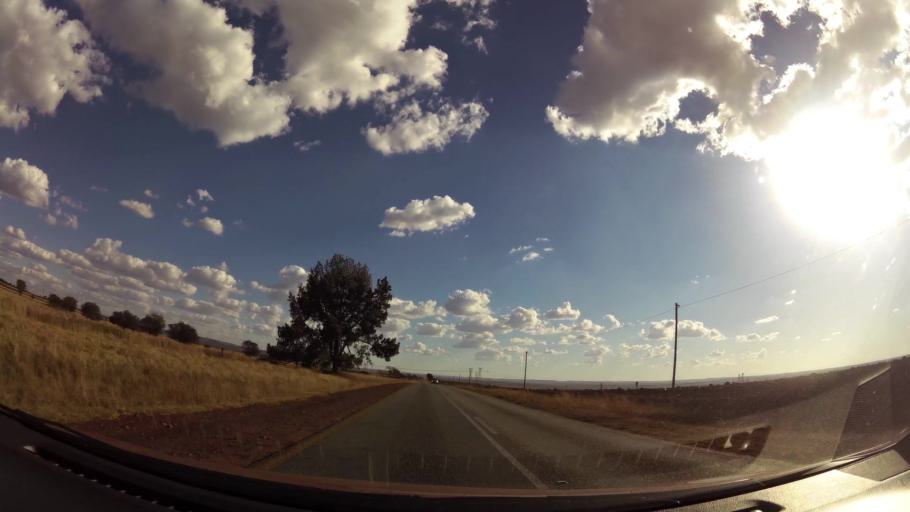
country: ZA
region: Gauteng
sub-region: West Rand District Municipality
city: Carletonville
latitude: -26.3959
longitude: 27.3105
